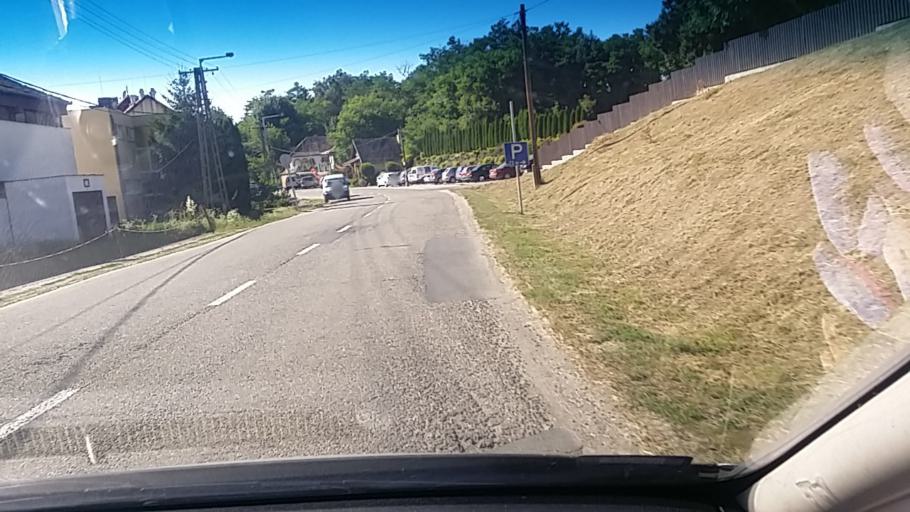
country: HU
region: Nograd
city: Retsag
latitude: 47.9224
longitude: 19.1808
